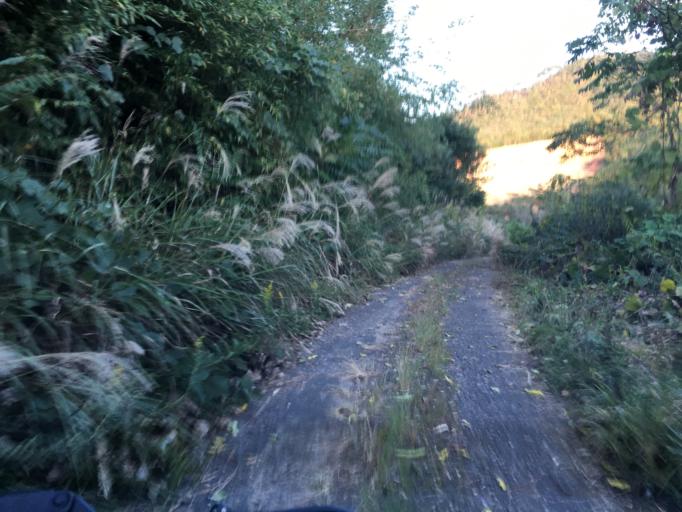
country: JP
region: Fukushima
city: Yanagawamachi-saiwaicho
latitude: 37.8402
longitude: 140.6306
